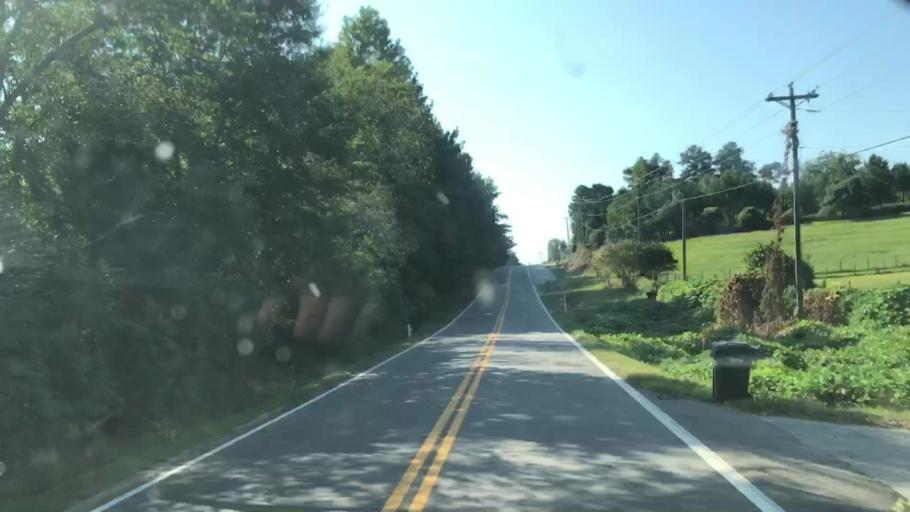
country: US
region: Georgia
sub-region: Barrow County
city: Auburn
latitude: 33.9159
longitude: -83.8201
